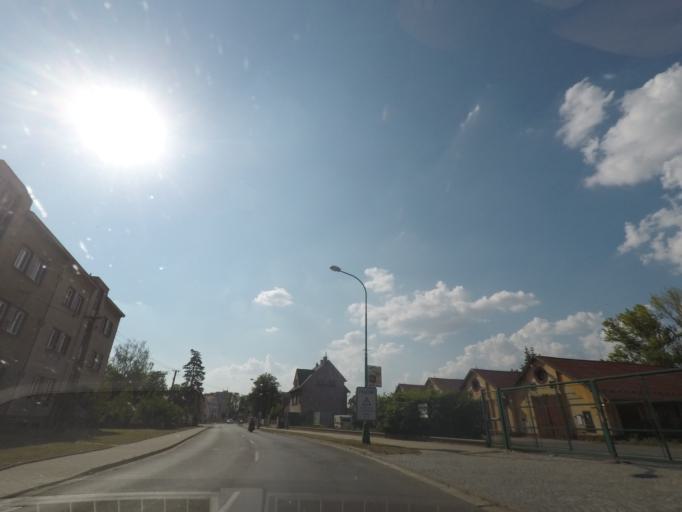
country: CZ
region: Kralovehradecky
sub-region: Okres Nachod
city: Jaromer
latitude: 50.3452
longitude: 15.9211
